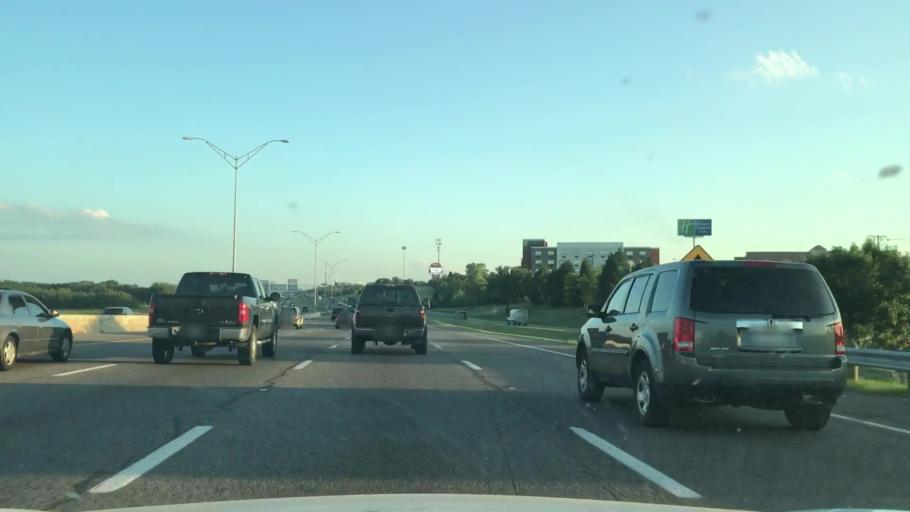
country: US
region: Texas
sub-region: Dallas County
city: Mesquite
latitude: 32.7670
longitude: -96.6221
